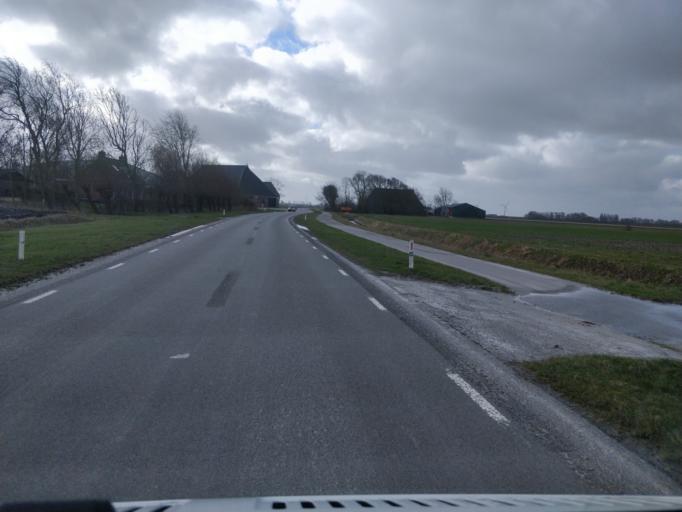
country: NL
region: Friesland
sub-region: Gemeente Franekeradeel
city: Sexbierum
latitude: 53.2091
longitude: 5.4642
